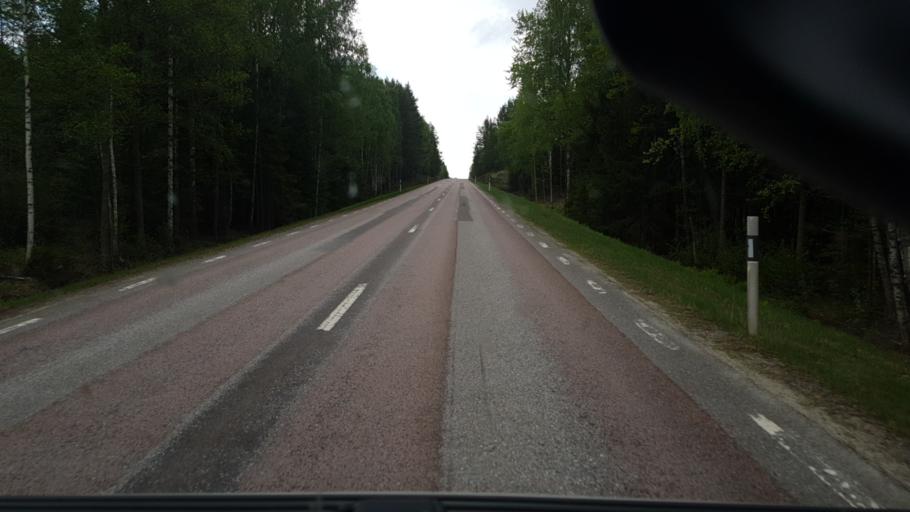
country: SE
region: Vaermland
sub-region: Arvika Kommun
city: Arvika
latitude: 59.5716
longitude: 12.7144
